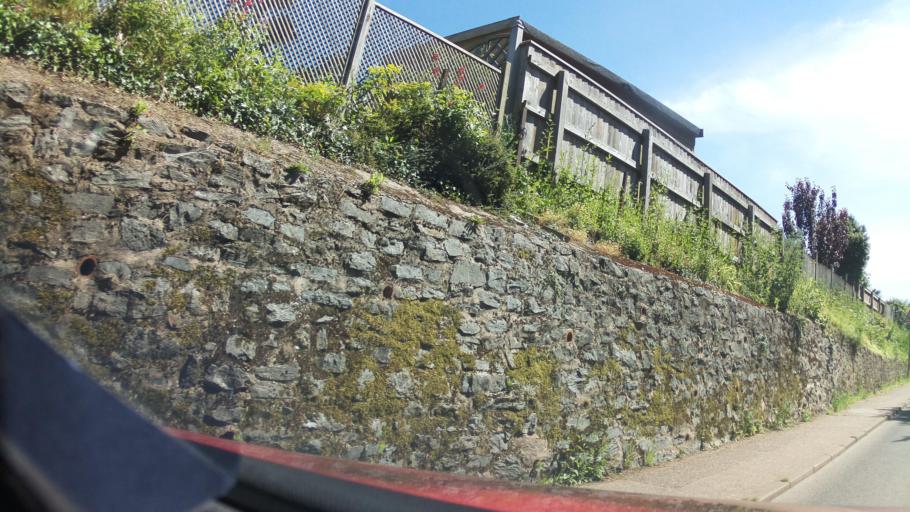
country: GB
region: England
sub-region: Devon
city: Ottery St Mary
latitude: 50.7520
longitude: -3.2707
